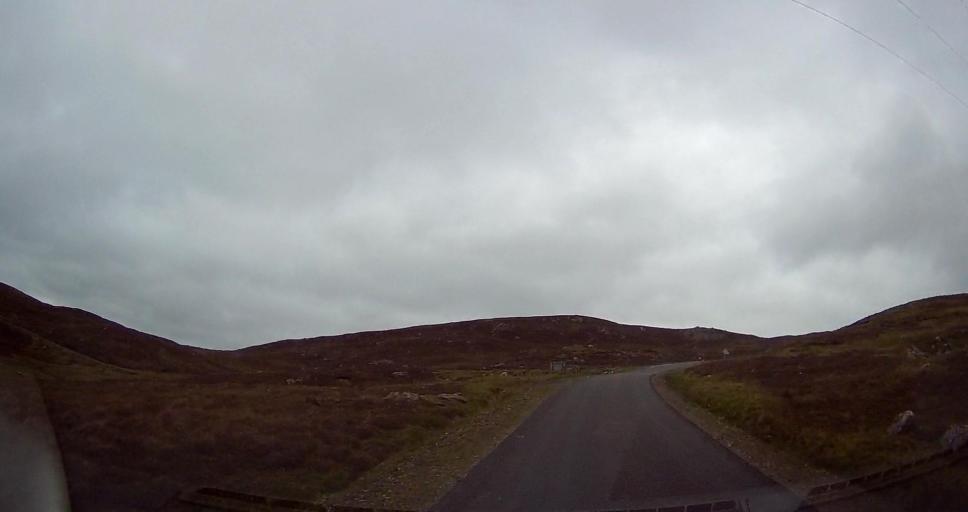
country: GB
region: Scotland
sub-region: Shetland Islands
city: Lerwick
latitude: 60.3396
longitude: -1.3177
